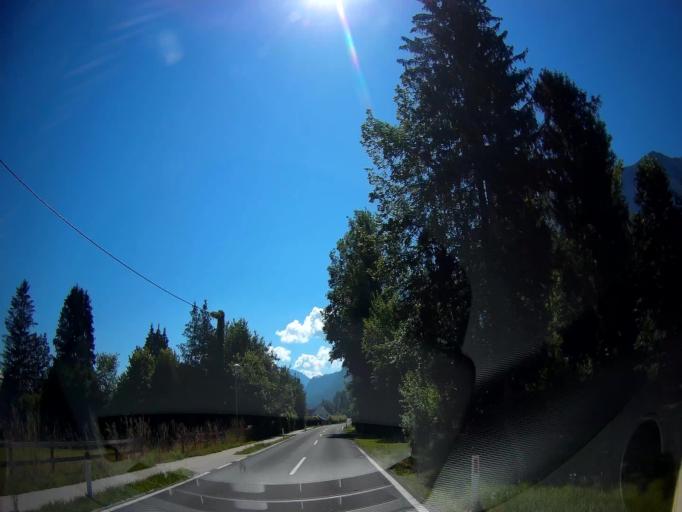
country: AT
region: Carinthia
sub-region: Politischer Bezirk Volkermarkt
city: Gallizien
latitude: 46.5466
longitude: 14.5161
